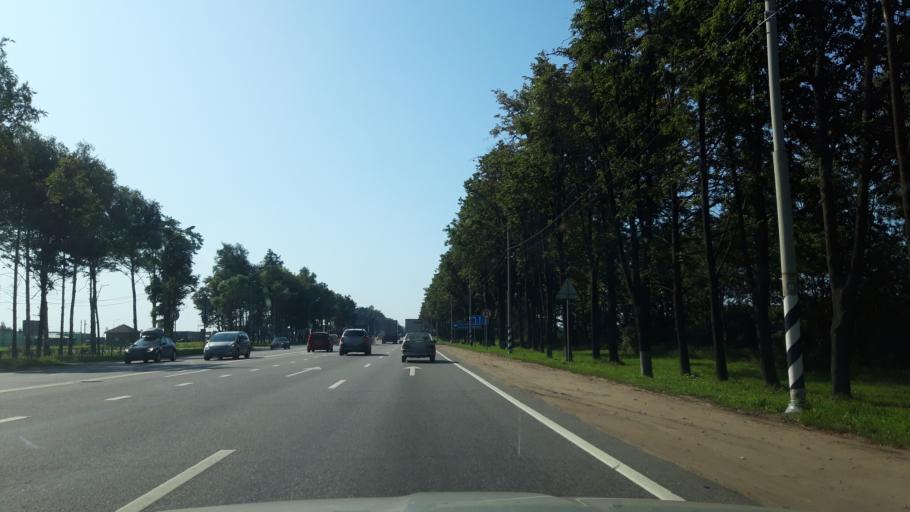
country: RU
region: Tverskaya
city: Zavidovo
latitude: 56.5771
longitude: 36.4967
